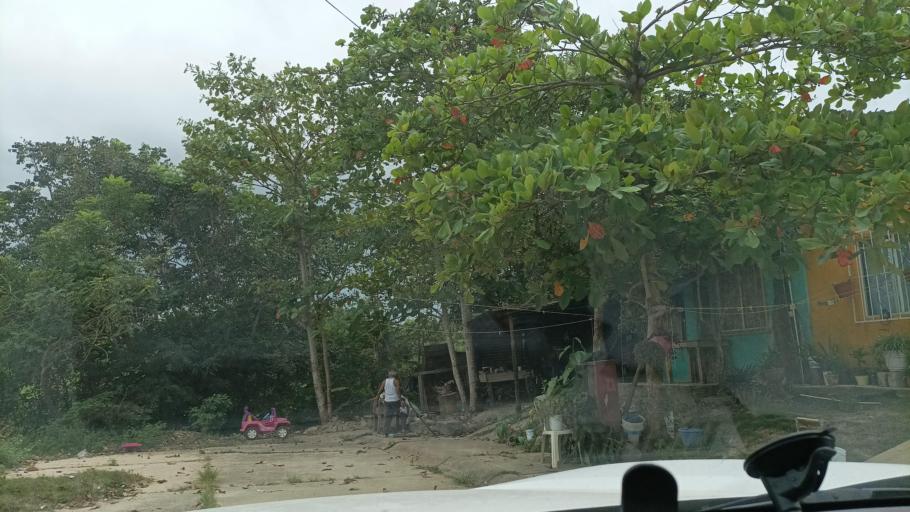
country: MX
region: Veracruz
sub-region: Soconusco
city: Fraccionamiento Santa Cruz
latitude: 17.9710
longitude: -94.8965
